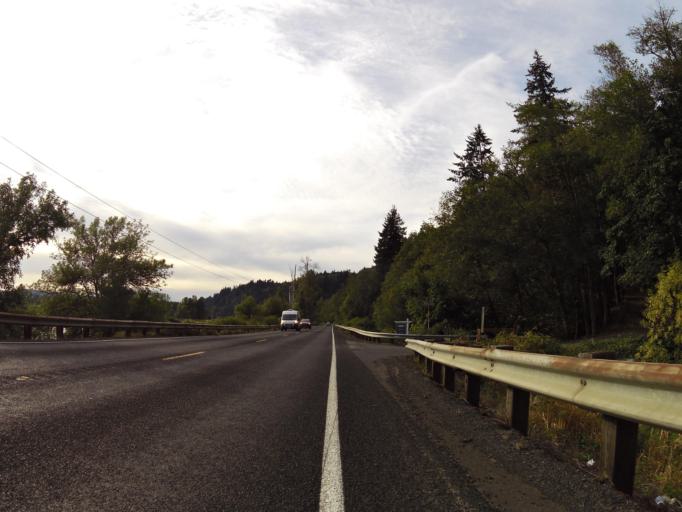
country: US
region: Washington
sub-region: Cowlitz County
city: West Longview
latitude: 46.1851
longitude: -123.0812
